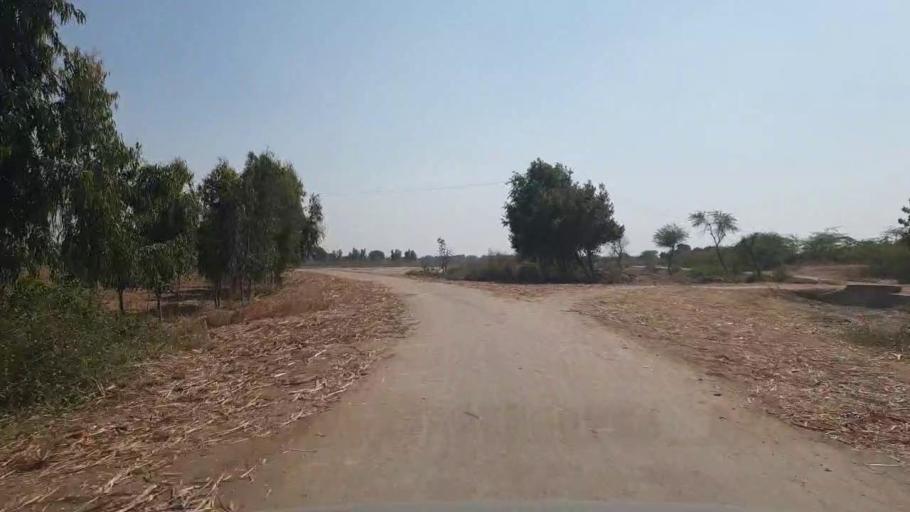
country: PK
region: Sindh
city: Digri
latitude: 25.0950
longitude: 69.2491
